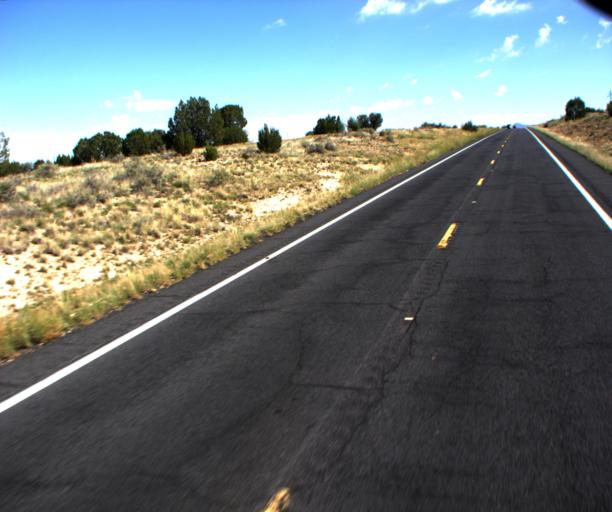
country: US
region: Arizona
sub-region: Coconino County
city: Williams
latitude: 35.5874
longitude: -112.1506
